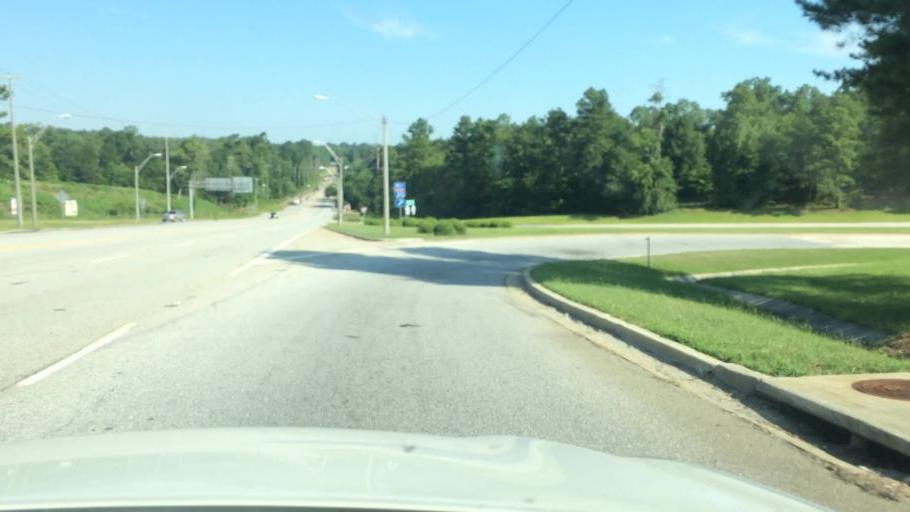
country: US
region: South Carolina
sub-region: Aiken County
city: North Augusta
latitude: 33.5408
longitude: -81.9925
